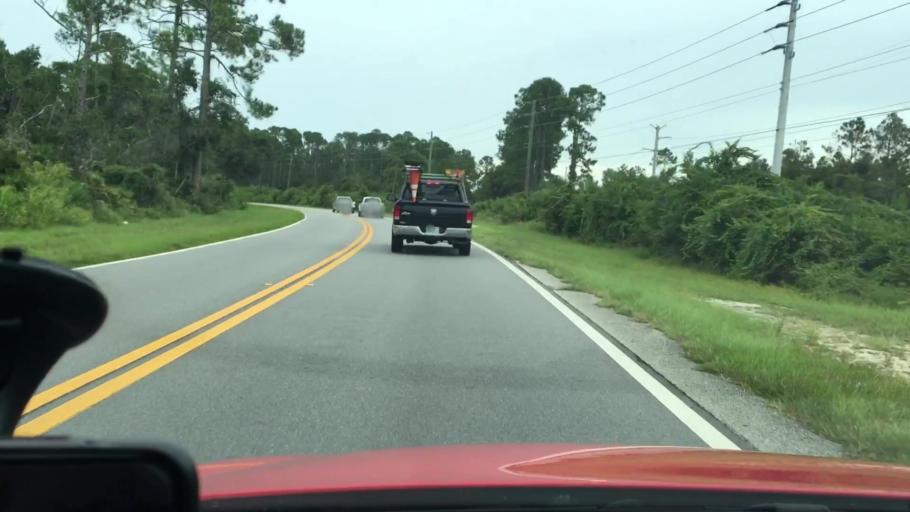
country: US
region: Florida
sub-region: Flagler County
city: Palm Coast
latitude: 29.5110
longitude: -81.1948
